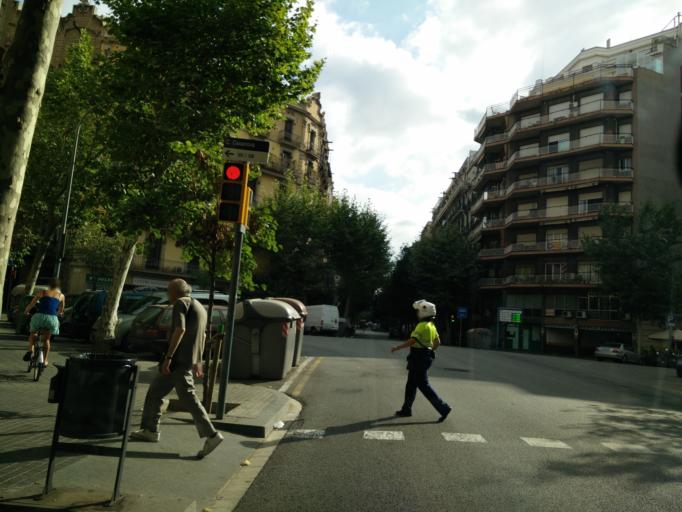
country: ES
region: Catalonia
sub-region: Provincia de Barcelona
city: Barcelona
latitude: 41.3871
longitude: 2.1558
